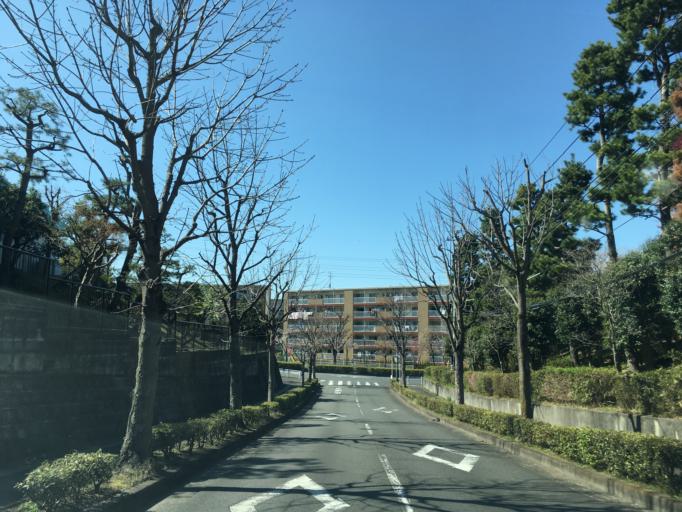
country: JP
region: Tokyo
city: Hino
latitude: 35.6297
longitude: 139.4147
